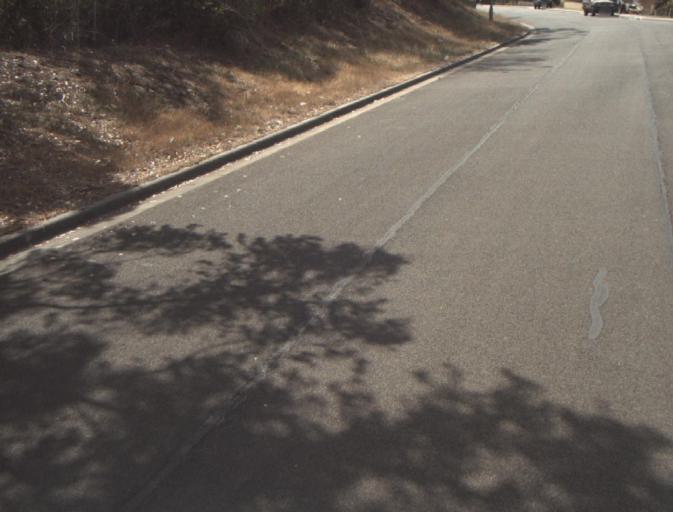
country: AU
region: Tasmania
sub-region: Launceston
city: Newstead
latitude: -41.4156
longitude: 147.1816
